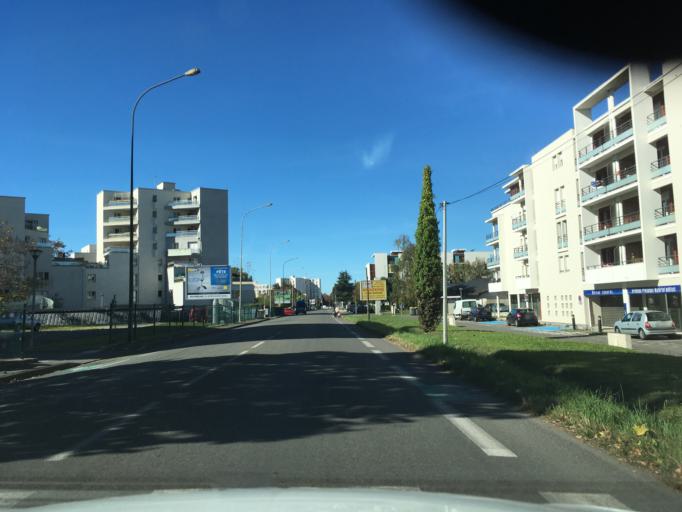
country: FR
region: Aquitaine
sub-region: Departement des Pyrenees-Atlantiques
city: Pau
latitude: 43.3216
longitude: -0.3614
